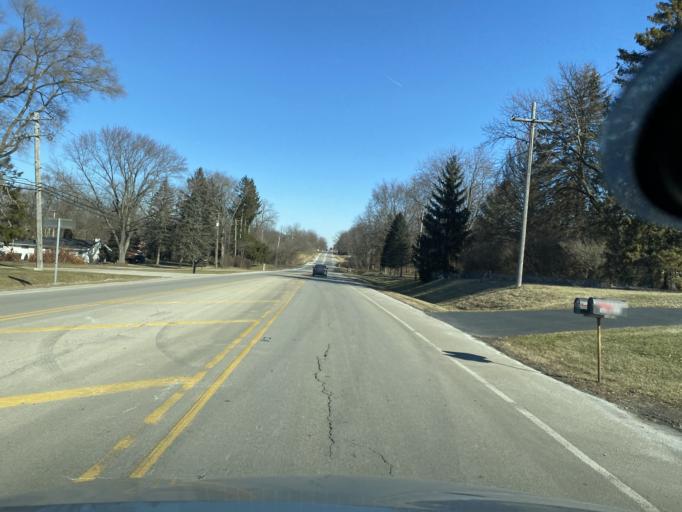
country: US
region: Illinois
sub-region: Will County
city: Lockport
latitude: 41.6133
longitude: -88.0391
